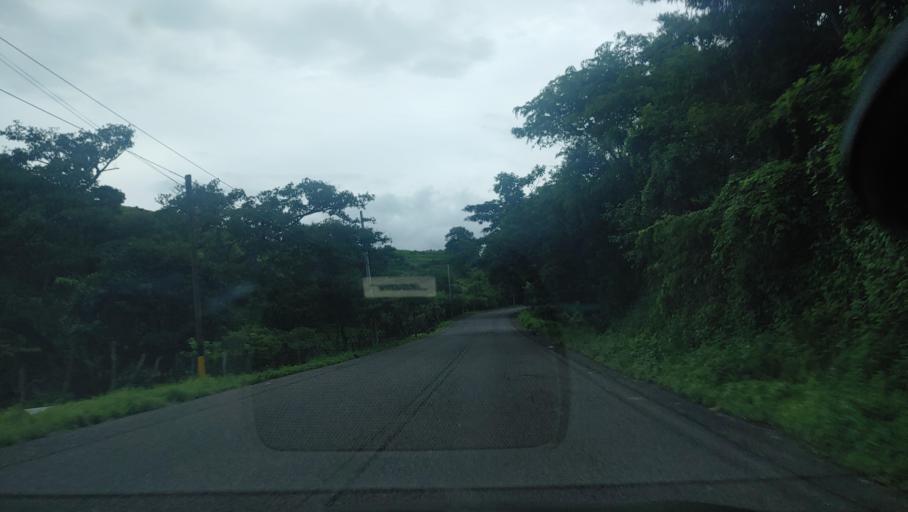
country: HN
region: Choluteca
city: Corpus
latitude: 13.3698
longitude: -87.0022
